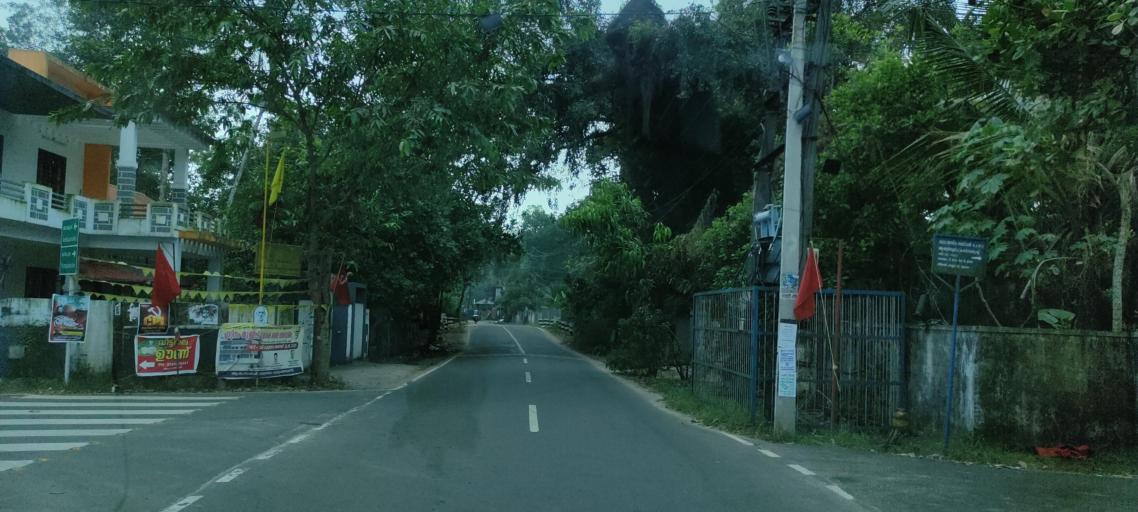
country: IN
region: Kerala
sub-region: Alappuzha
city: Alleppey
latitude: 9.5761
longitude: 76.3396
